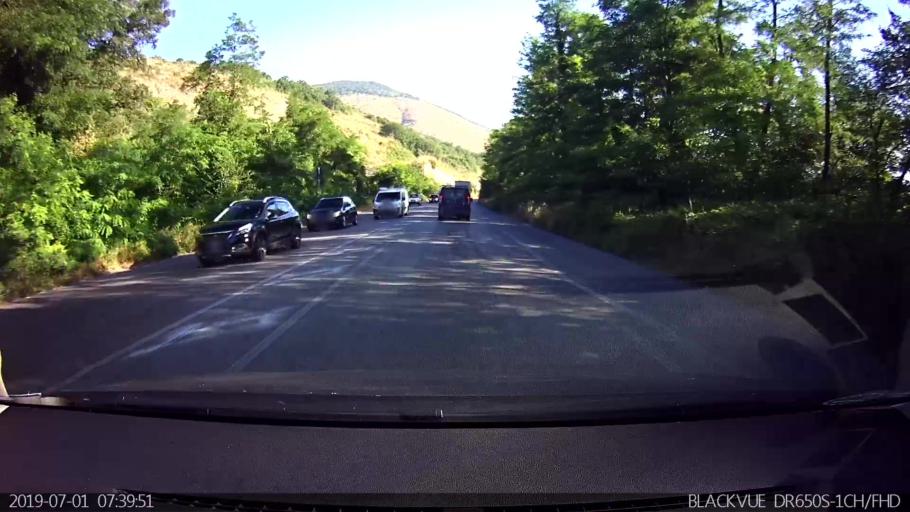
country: IT
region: Latium
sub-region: Provincia di Frosinone
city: Giuliano di Roma
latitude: 41.5528
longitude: 13.2672
